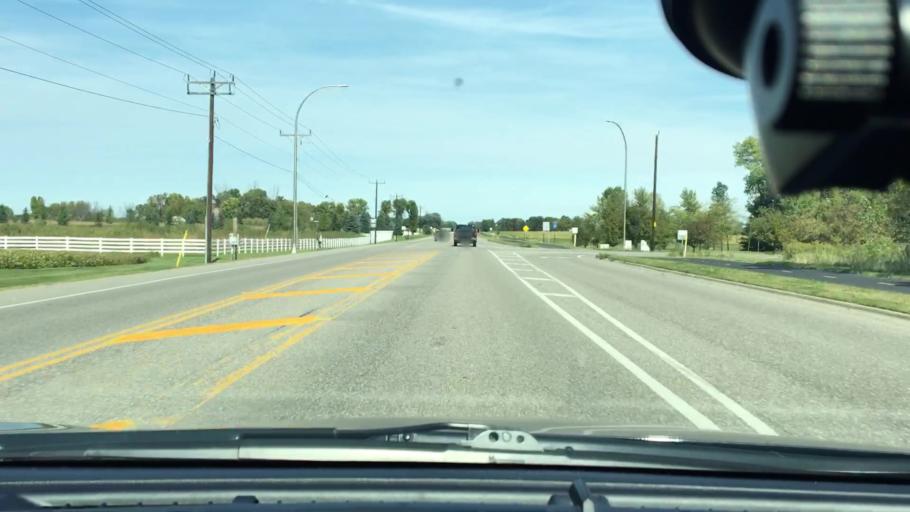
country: US
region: Minnesota
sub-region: Wright County
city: Hanover
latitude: 45.1303
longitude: -93.6357
